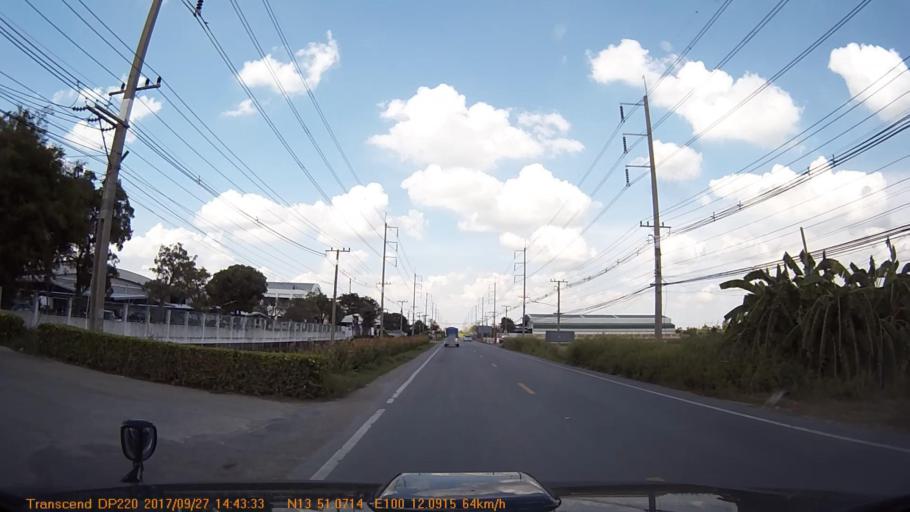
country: TH
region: Nakhon Pathom
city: Nakhon Chai Si
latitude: 13.8512
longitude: 100.2015
